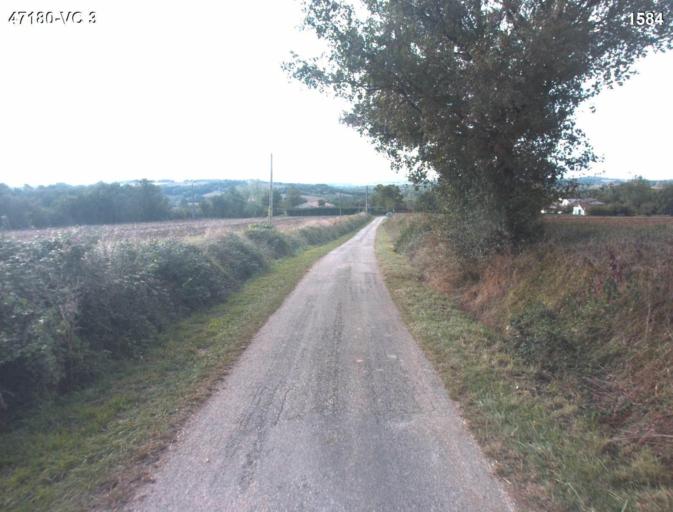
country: FR
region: Aquitaine
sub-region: Departement du Lot-et-Garonne
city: Sainte-Colombe-en-Bruilhois
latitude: 44.1553
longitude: 0.4425
